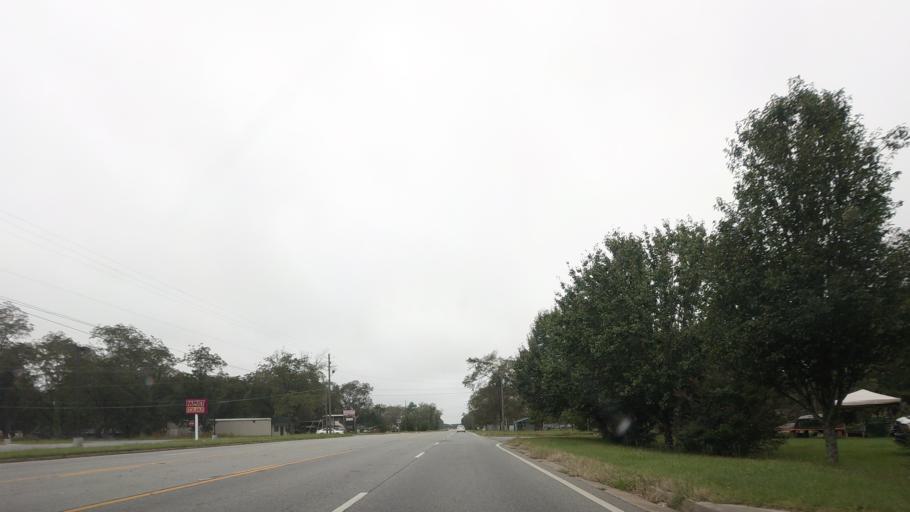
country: US
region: Georgia
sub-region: Berrien County
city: Enigma
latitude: 31.3865
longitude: -83.2248
